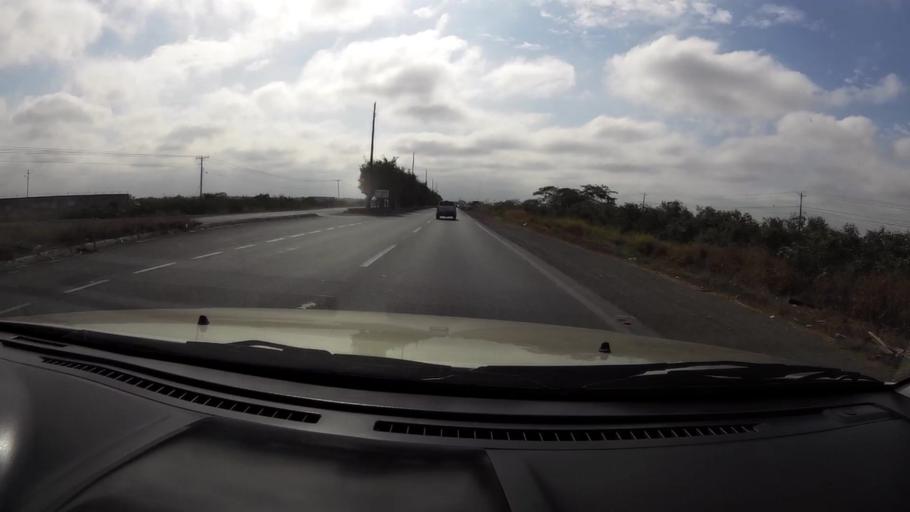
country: EC
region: Guayas
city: Eloy Alfaro
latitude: -2.1919
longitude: -79.7939
